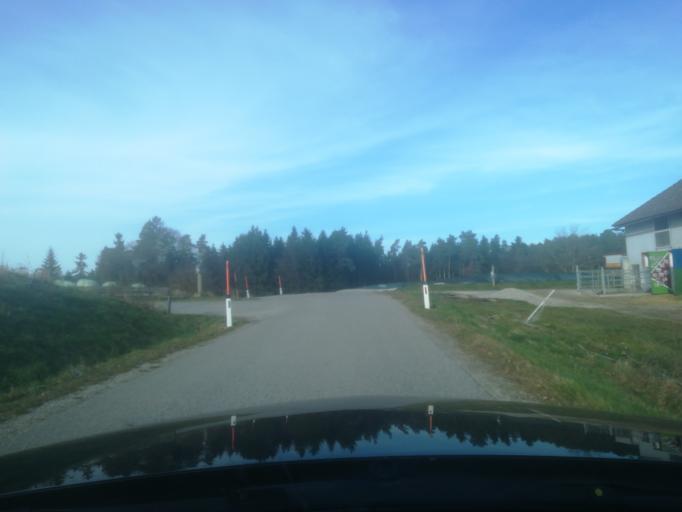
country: AT
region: Upper Austria
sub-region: Politischer Bezirk Perg
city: Perg
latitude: 48.3270
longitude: 14.6538
